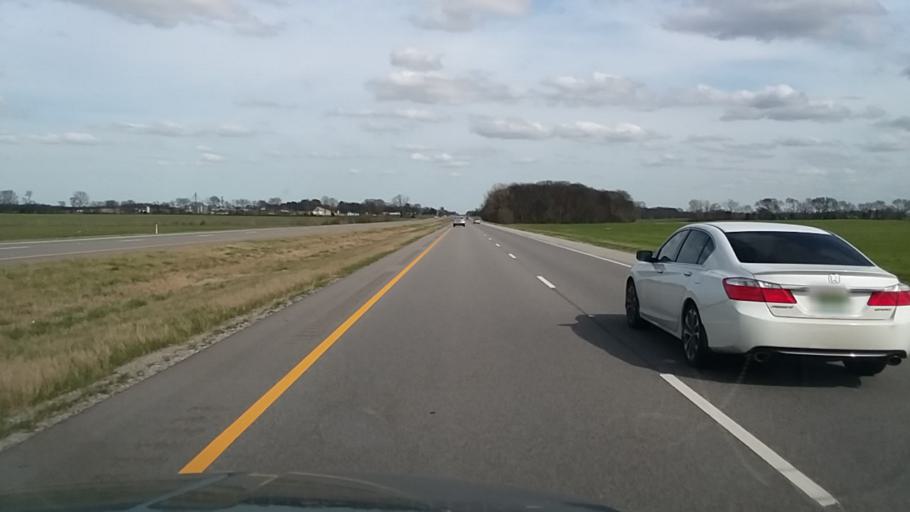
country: US
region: Alabama
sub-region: Colbert County
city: Muscle Shoals
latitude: 34.6850
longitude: -87.5800
